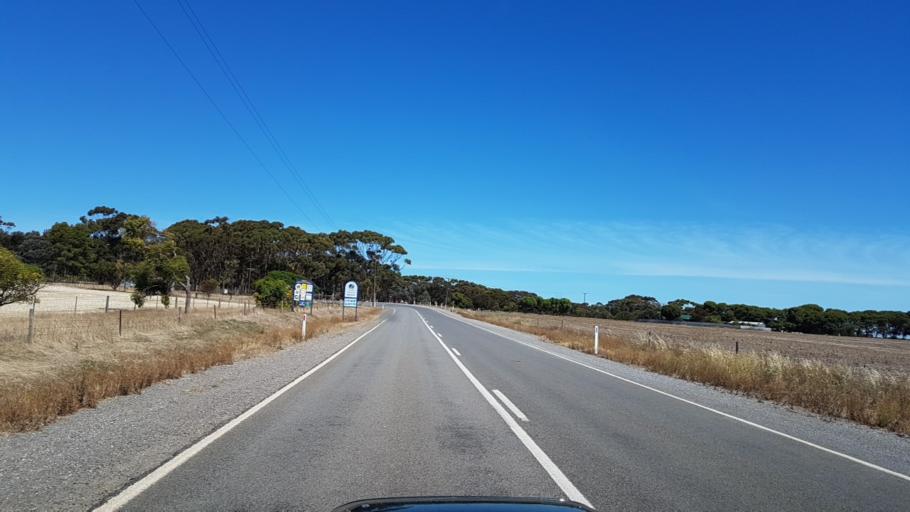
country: AU
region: South Australia
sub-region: Yorke Peninsula
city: Maitland
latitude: -34.3668
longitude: 137.6692
